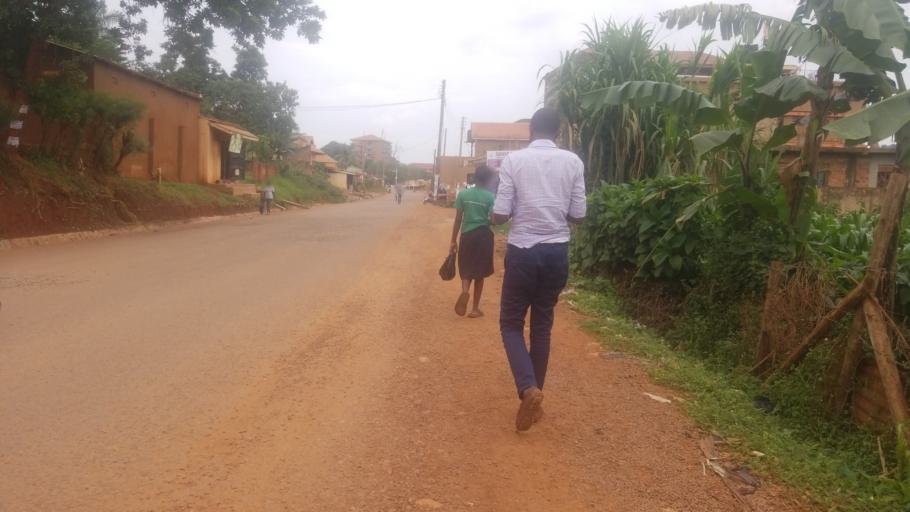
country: UG
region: Central Region
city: Kampala Central Division
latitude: 0.3340
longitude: 32.5623
